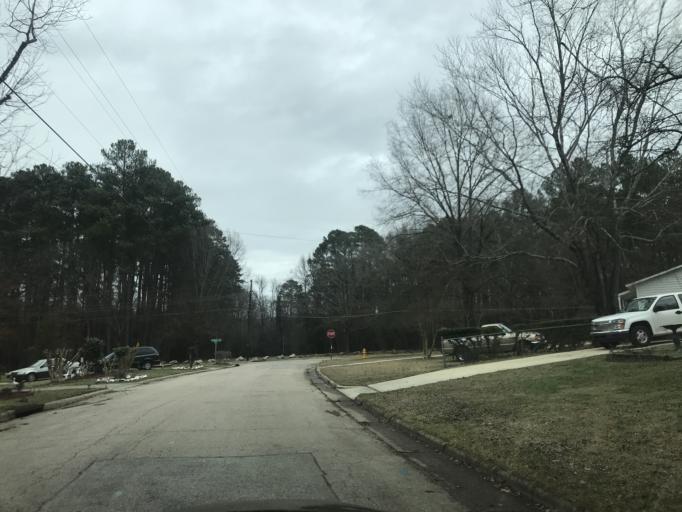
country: US
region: North Carolina
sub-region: Wake County
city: Raleigh
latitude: 35.7942
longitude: -78.5989
